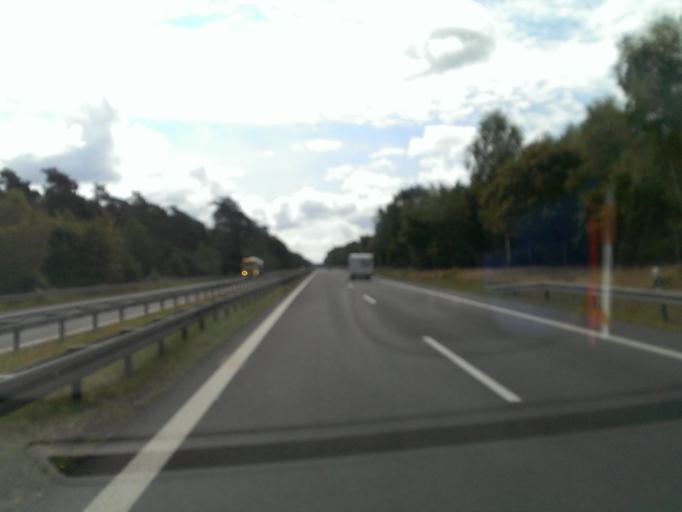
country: DE
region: Brandenburg
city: Bronkow
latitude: 51.7322
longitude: 13.8709
